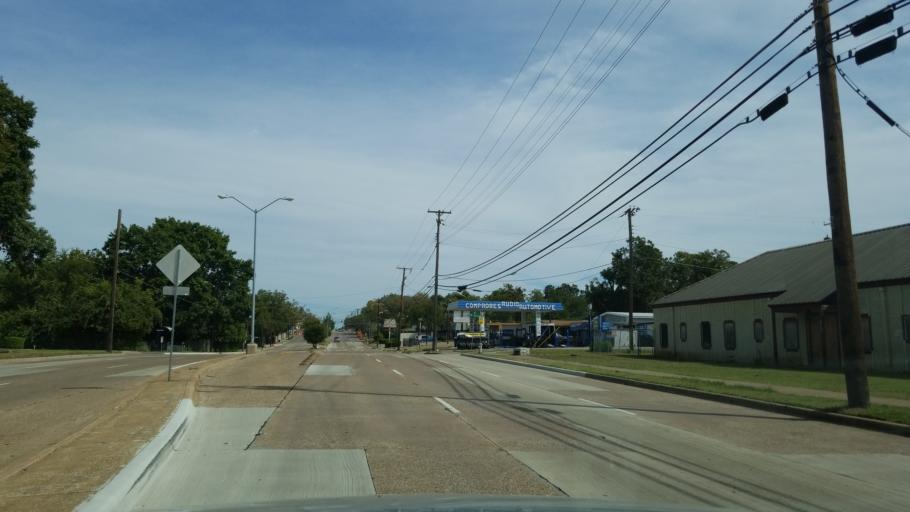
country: US
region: Texas
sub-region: Dallas County
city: Highland Park
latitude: 32.7988
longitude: -96.7175
